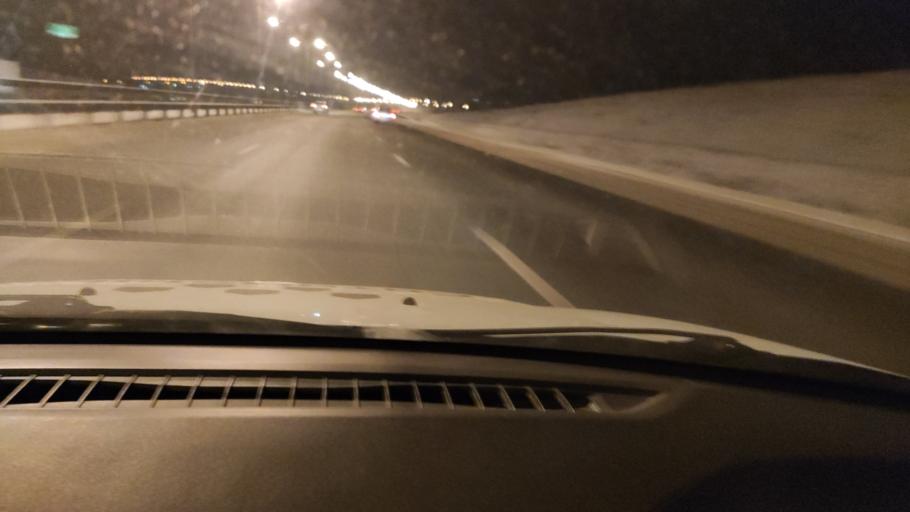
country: RU
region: Perm
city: Zvezdnyy
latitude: 57.7684
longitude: 56.3352
